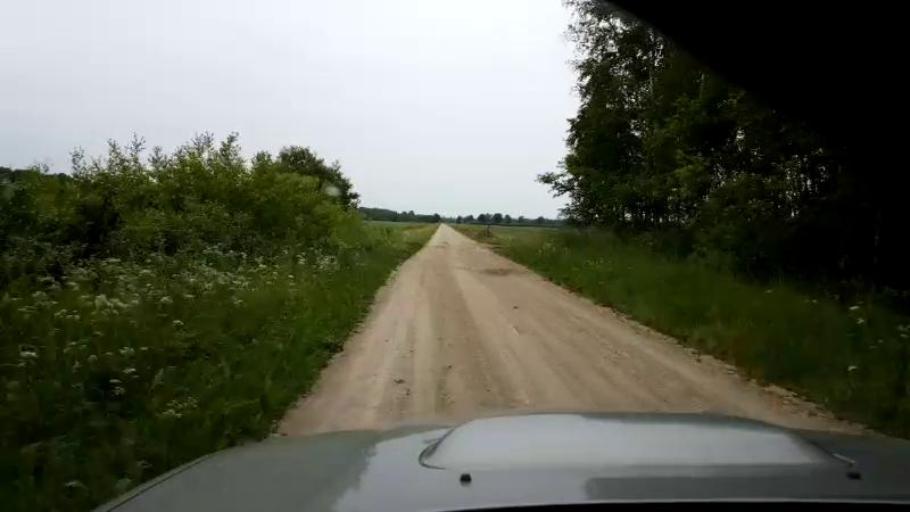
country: EE
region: Paernumaa
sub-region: Halinga vald
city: Parnu-Jaagupi
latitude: 58.5500
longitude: 24.6252
